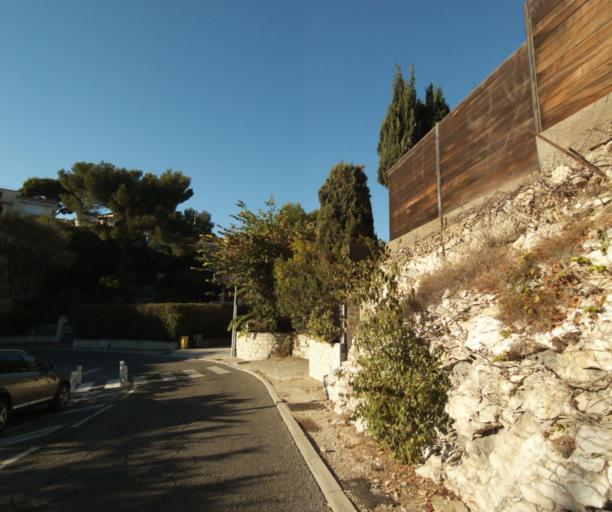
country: FR
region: Provence-Alpes-Cote d'Azur
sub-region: Departement des Bouches-du-Rhone
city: Cassis
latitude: 43.2207
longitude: 5.5409
